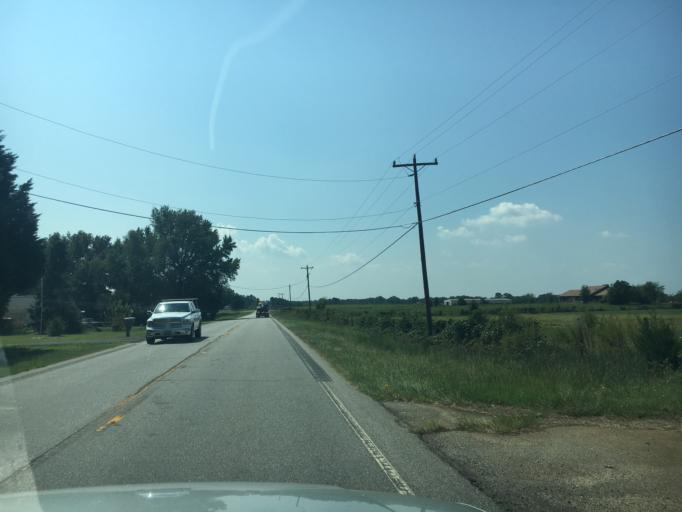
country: US
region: South Carolina
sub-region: Anderson County
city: Centerville
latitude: 34.4984
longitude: -82.7742
